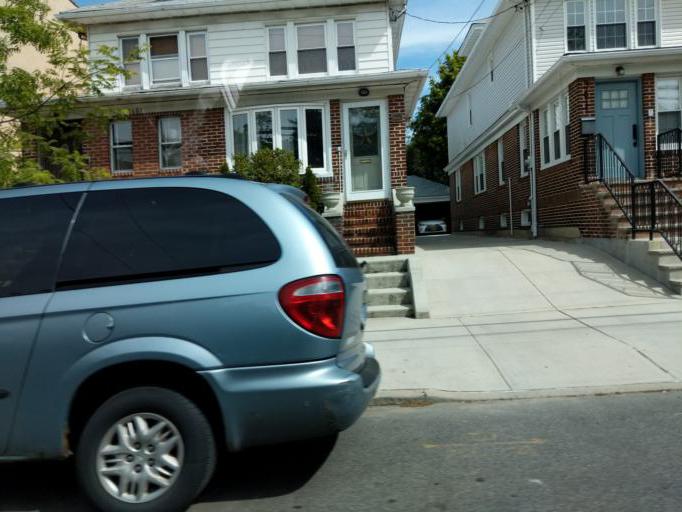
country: US
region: New York
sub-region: Kings County
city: Brooklyn
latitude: 40.6226
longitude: -73.9398
